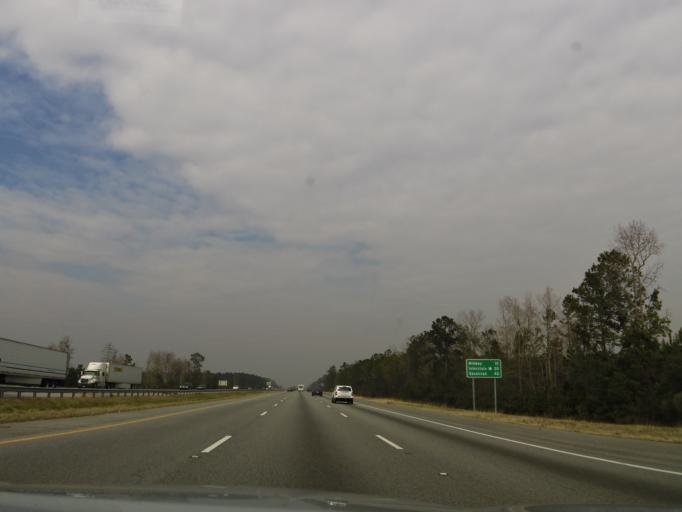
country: US
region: Georgia
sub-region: Liberty County
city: Midway
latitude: 31.6648
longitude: -81.3924
